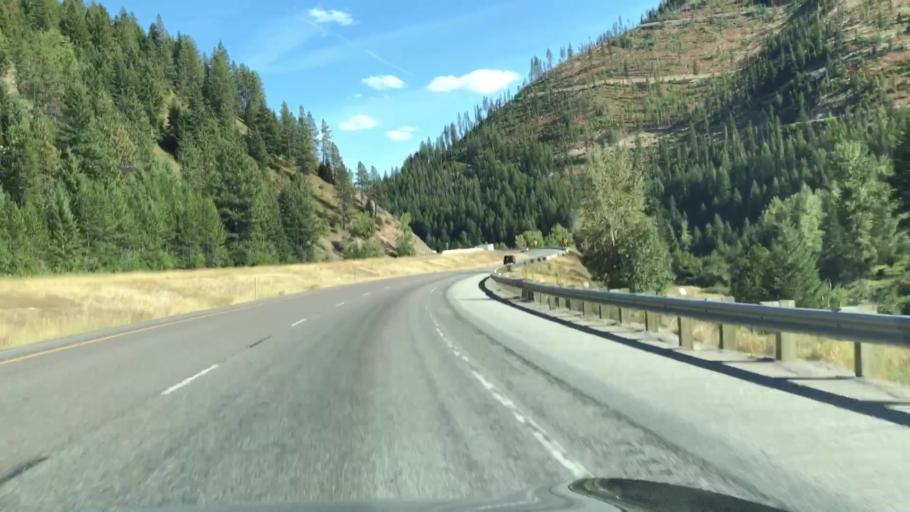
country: US
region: Montana
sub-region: Sanders County
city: Thompson Falls
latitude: 47.4034
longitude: -115.4758
